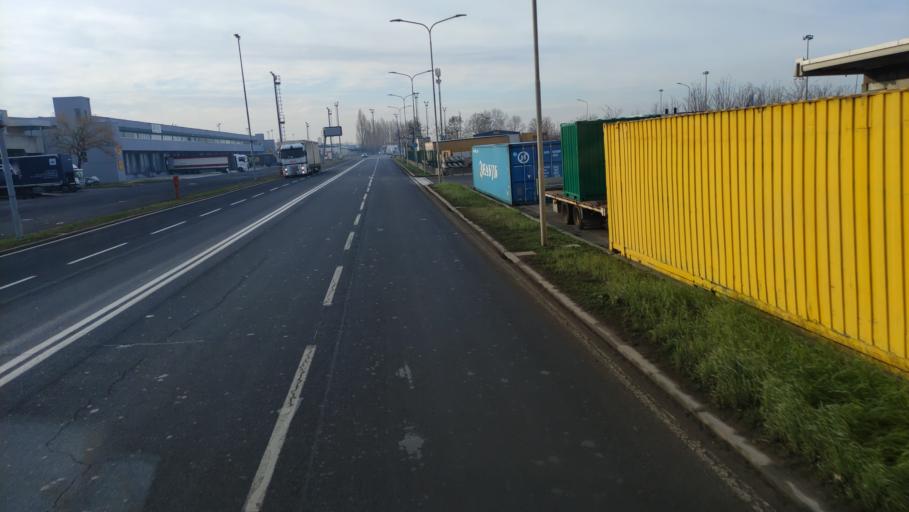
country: IT
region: Emilia-Romagna
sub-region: Provincia di Bologna
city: San Giorgio di Piano
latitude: 44.6259
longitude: 11.3800
